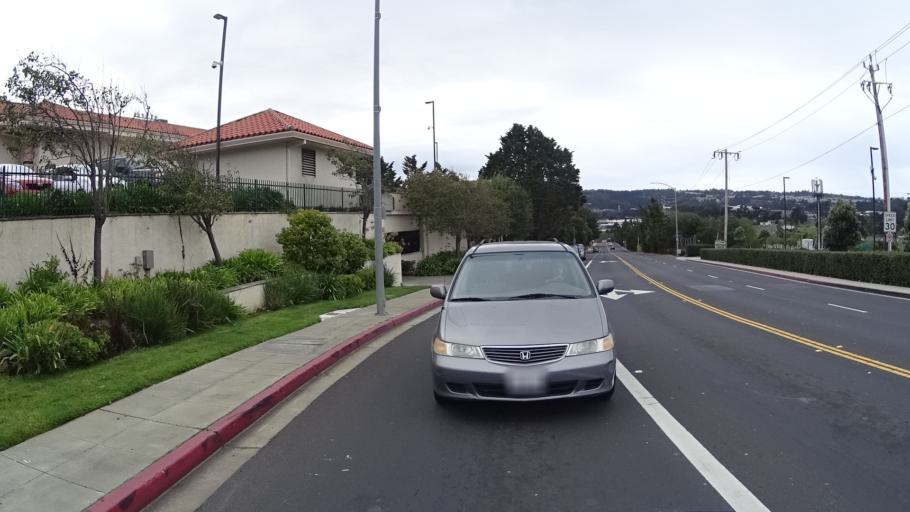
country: US
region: California
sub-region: San Mateo County
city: Colma
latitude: 37.6805
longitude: -122.4530
